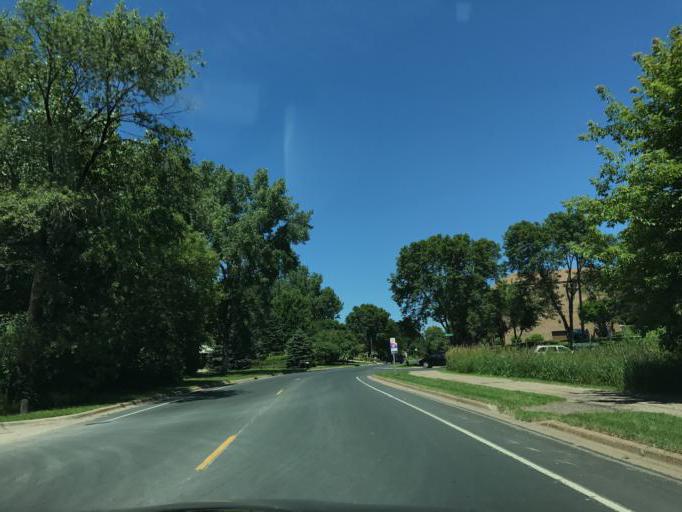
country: US
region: Minnesota
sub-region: Hennepin County
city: Osseo
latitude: 45.0794
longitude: -93.4054
